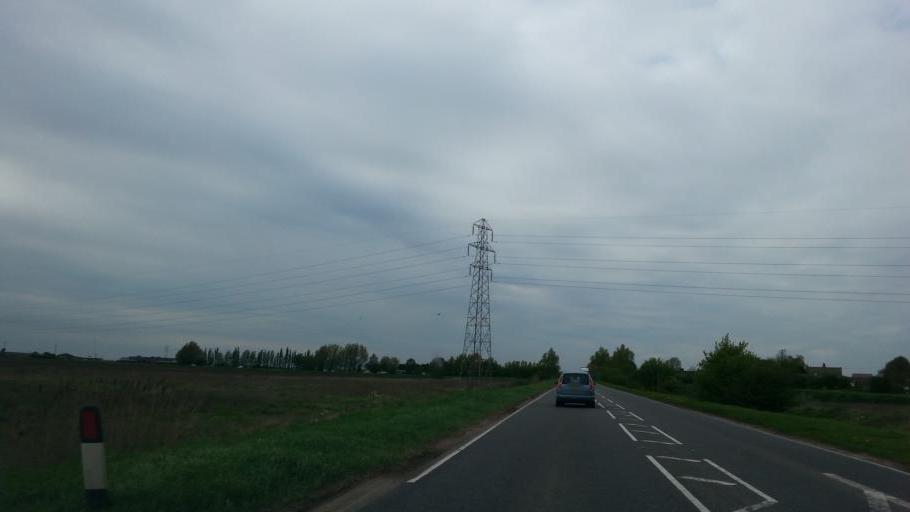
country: GB
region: England
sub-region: Cambridgeshire
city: March
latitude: 52.5499
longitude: 0.0693
